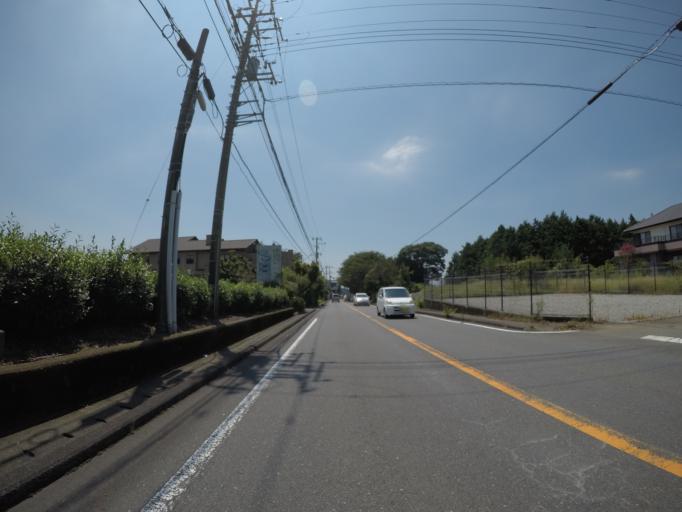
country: JP
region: Shizuoka
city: Fuji
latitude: 35.2037
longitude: 138.6843
